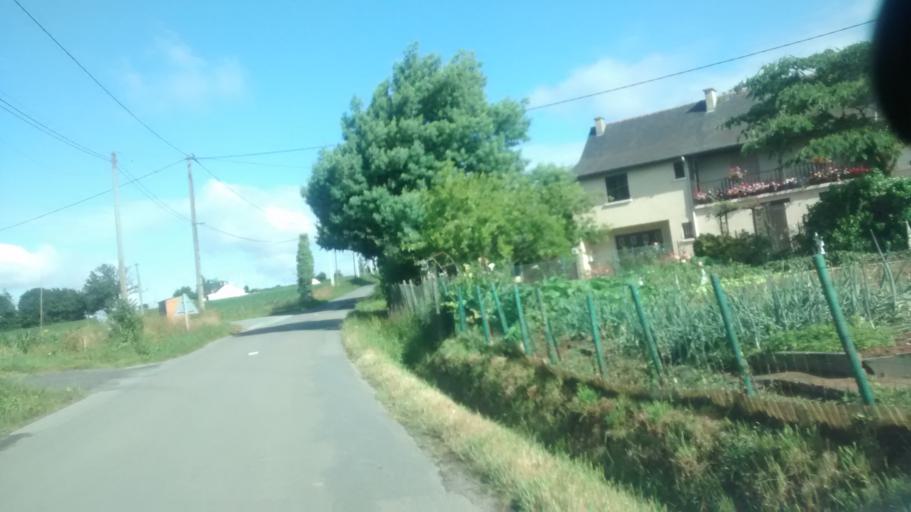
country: FR
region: Brittany
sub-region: Departement d'Ille-et-Vilaine
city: La Dominelais
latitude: 47.7841
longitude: -1.7025
